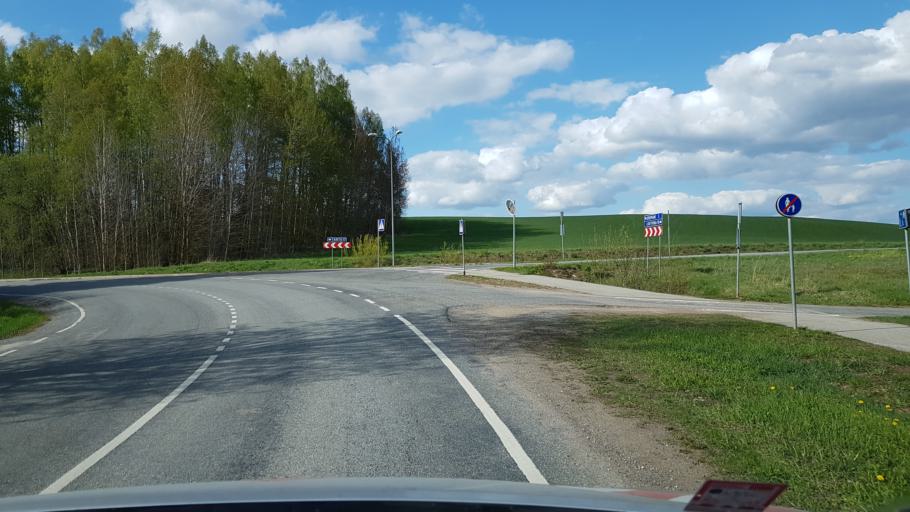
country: EE
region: Tartu
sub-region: UElenurme vald
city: Ulenurme
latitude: 58.2931
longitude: 26.8929
